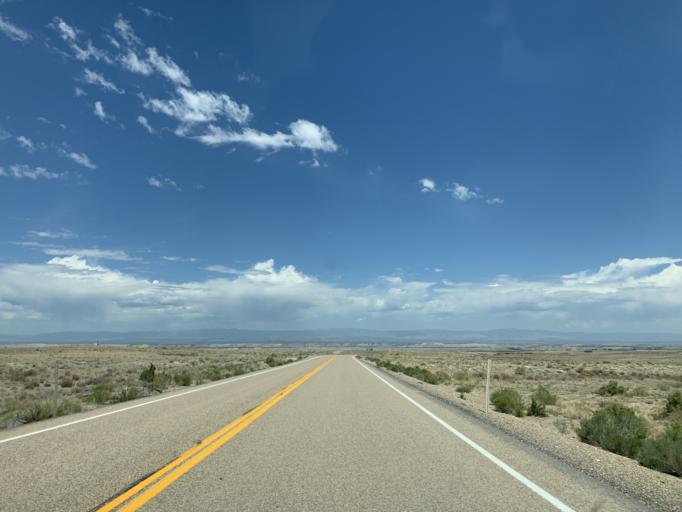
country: US
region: Utah
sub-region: Duchesne County
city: Duchesne
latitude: 40.0663
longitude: -110.1484
